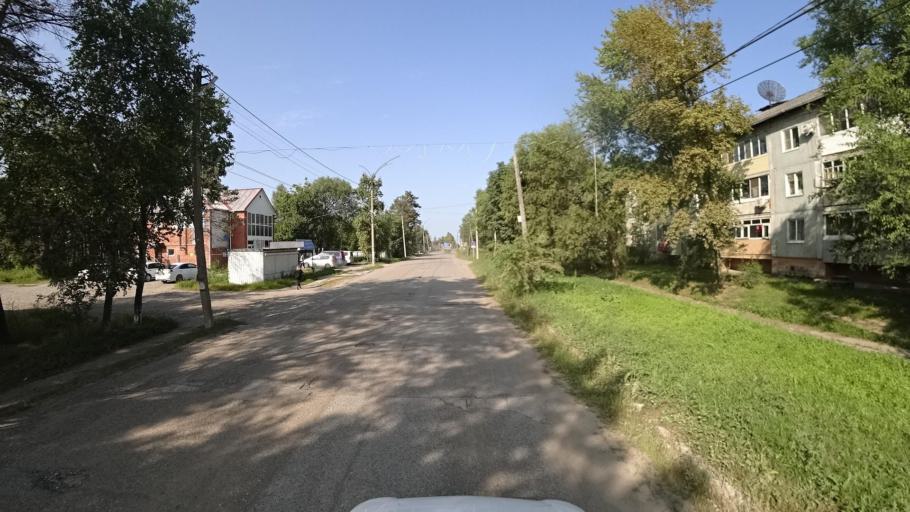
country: RU
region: Khabarovsk Krai
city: Khor
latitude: 47.9722
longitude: 135.0535
